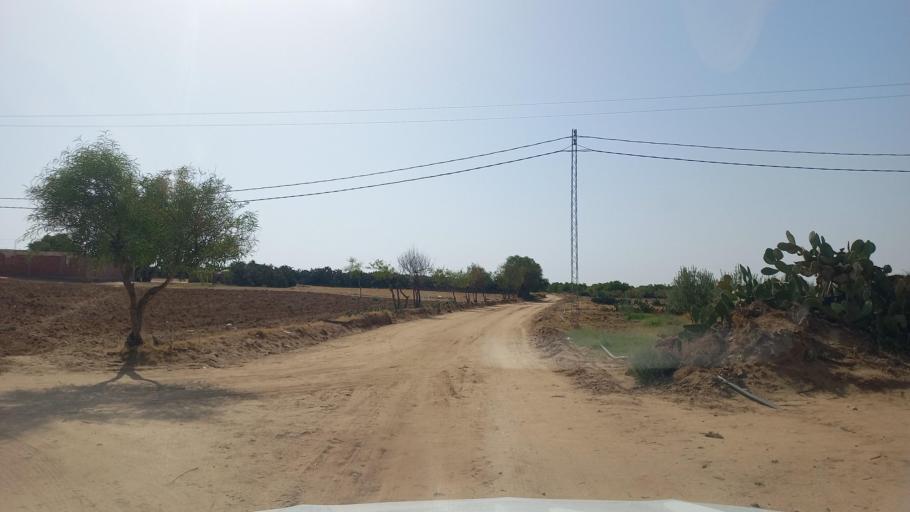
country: TN
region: Al Qasrayn
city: Kasserine
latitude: 35.2411
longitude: 9.0371
